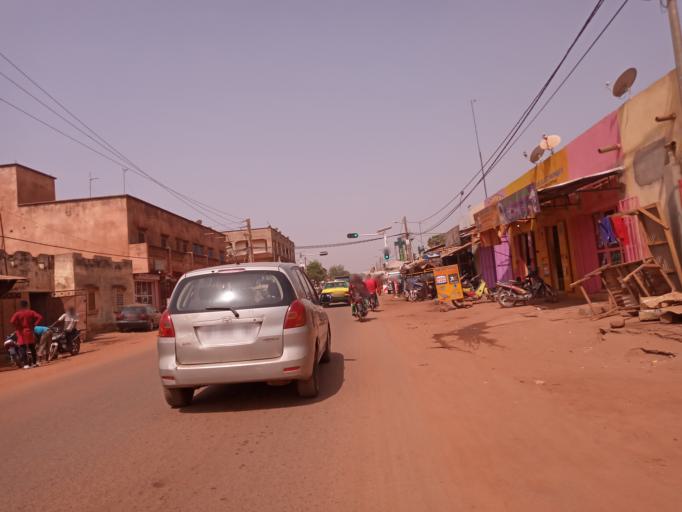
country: ML
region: Bamako
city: Bamako
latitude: 12.5888
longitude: -7.9819
